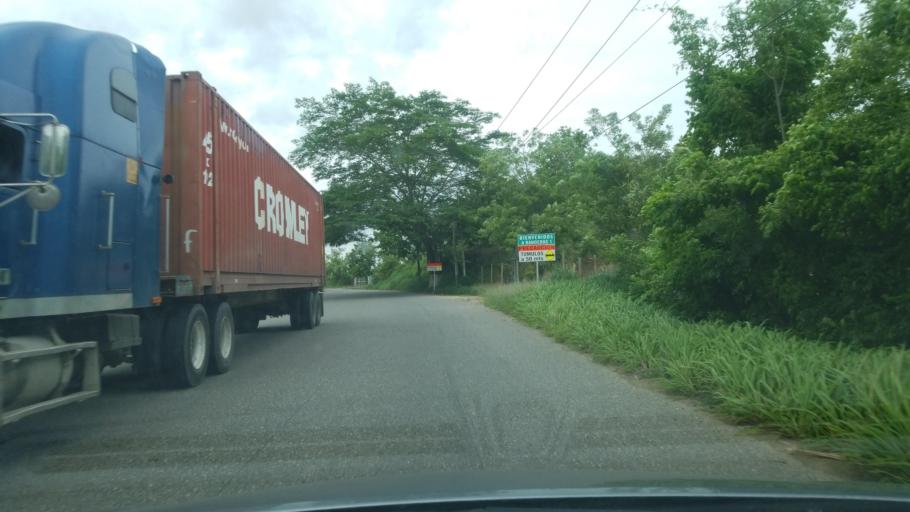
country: HN
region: Santa Barbara
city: La Flecha
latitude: 15.2993
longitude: -88.4567
